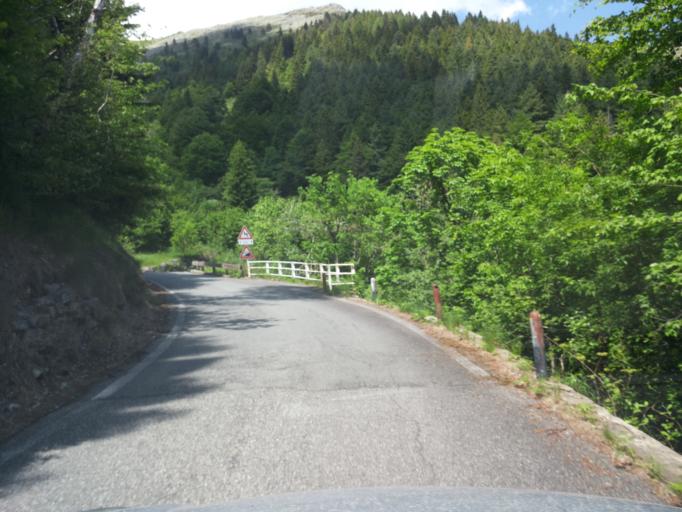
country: IT
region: Piedmont
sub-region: Provincia di Biella
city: Campiglia Cervo
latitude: 45.6370
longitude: 7.9776
